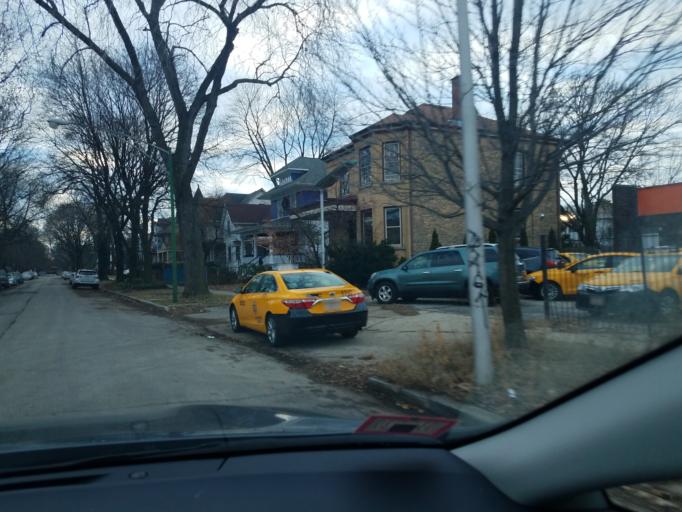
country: US
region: Illinois
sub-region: Cook County
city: Lincolnwood
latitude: 41.9599
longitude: -87.7357
